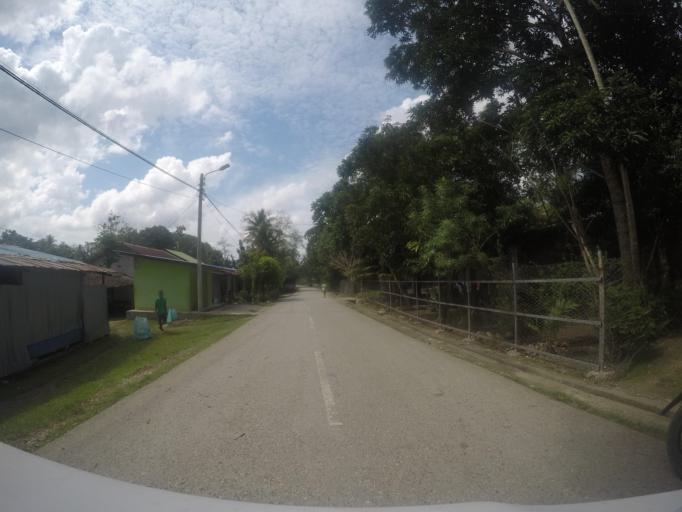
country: TL
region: Viqueque
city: Viqueque
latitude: -8.8514
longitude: 126.3644
